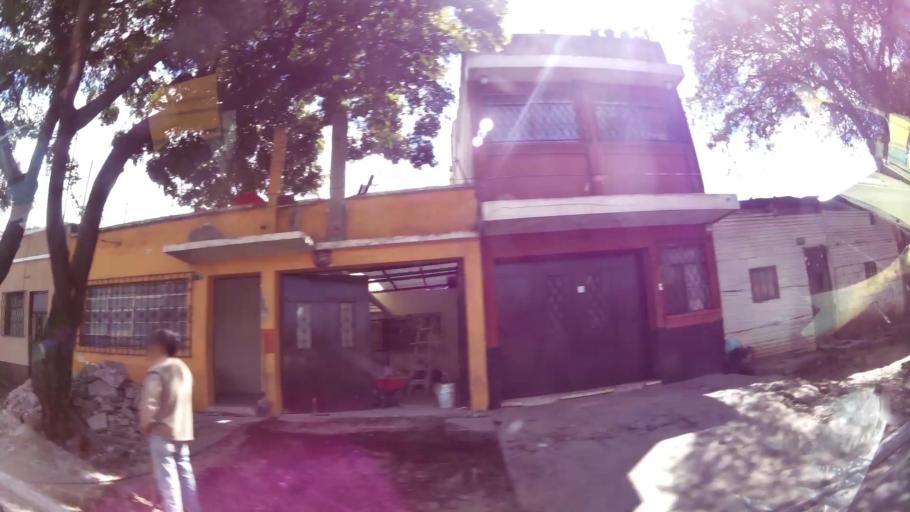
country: GT
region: Guatemala
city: Guatemala City
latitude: 14.5978
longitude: -90.5440
